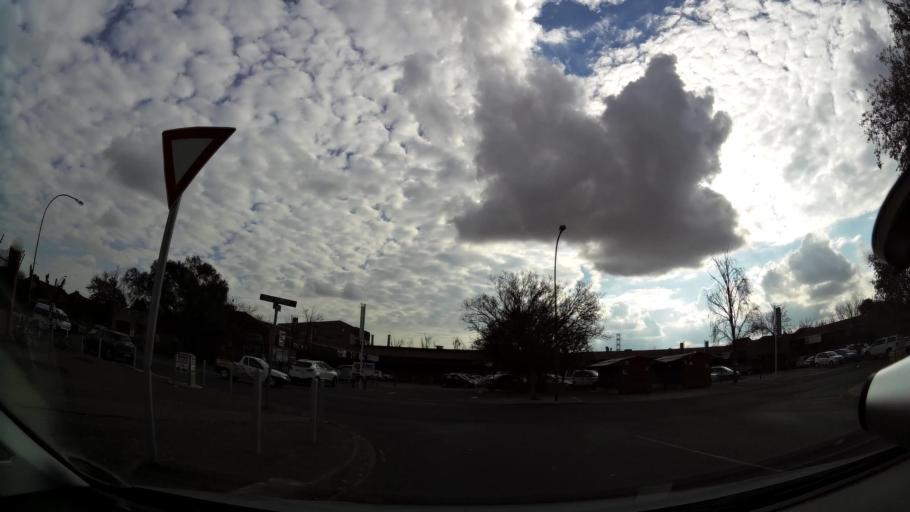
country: ZA
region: Orange Free State
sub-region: Mangaung Metropolitan Municipality
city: Bloemfontein
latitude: -29.0762
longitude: 26.1975
